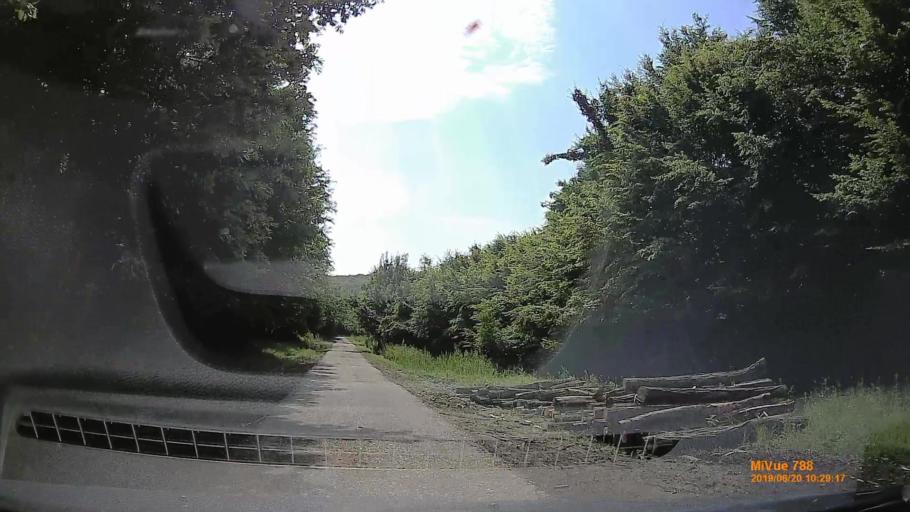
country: HU
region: Baranya
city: Mecseknadasd
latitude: 46.2088
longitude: 18.4926
